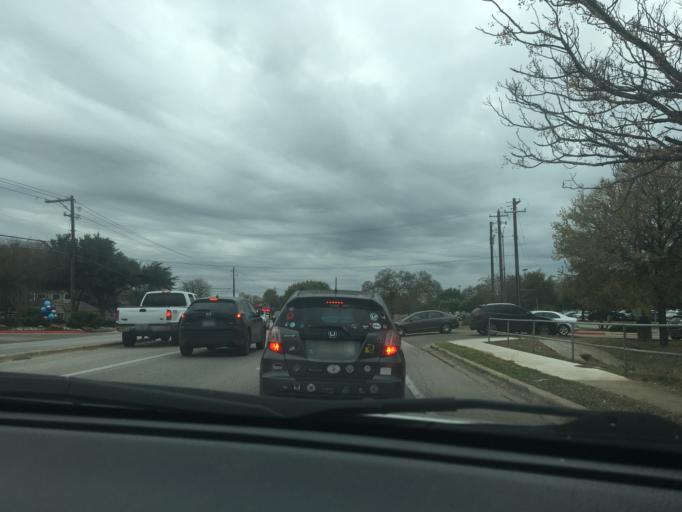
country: US
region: Texas
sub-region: Travis County
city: Shady Hollow
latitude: 30.2166
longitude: -97.8288
